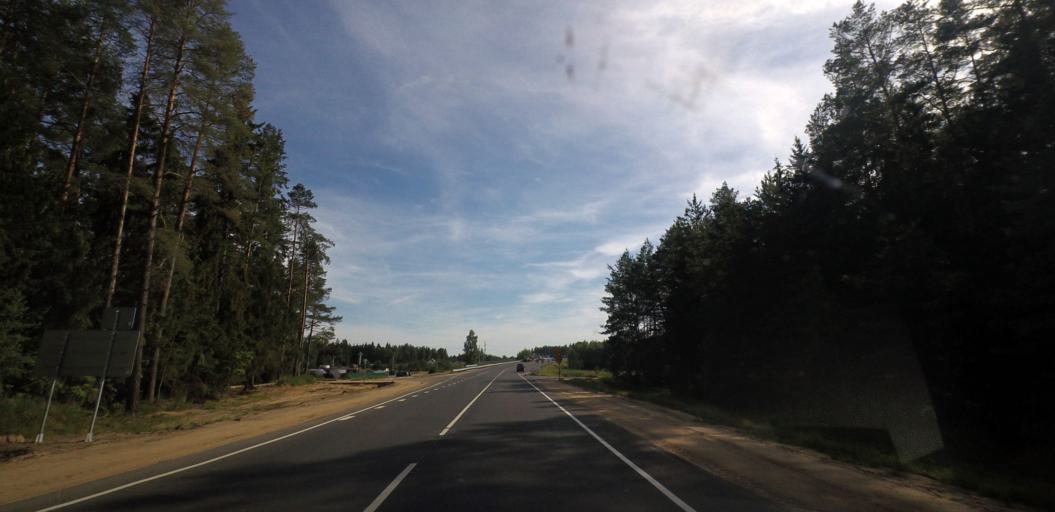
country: BY
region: Grodnenskaya
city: Iwye
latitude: 53.8875
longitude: 25.7431
